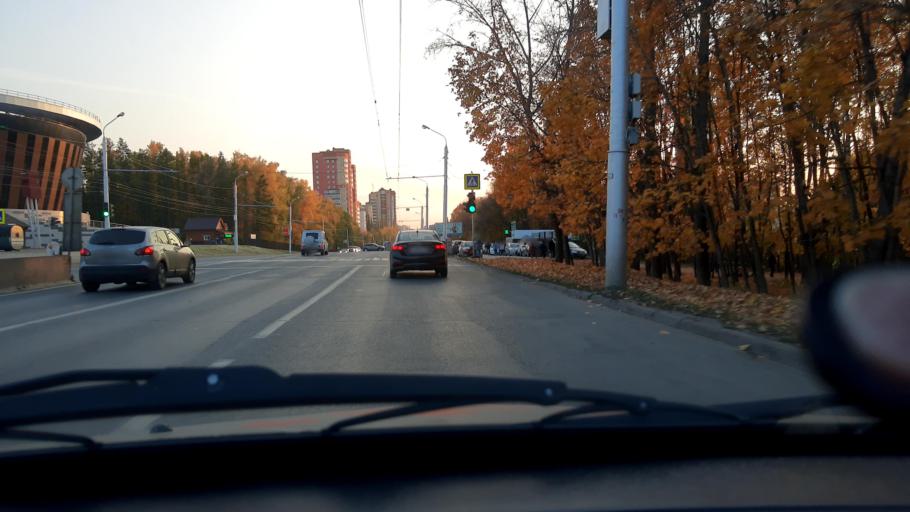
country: RU
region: Bashkortostan
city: Ufa
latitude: 54.7259
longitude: 56.0189
